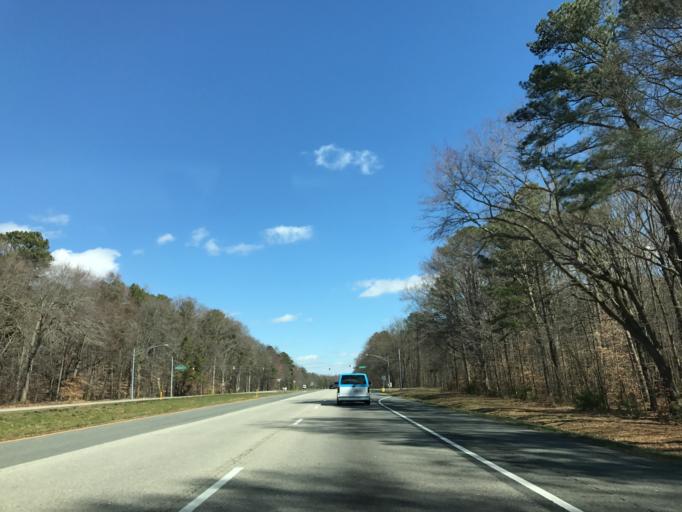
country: US
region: Maryland
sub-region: Queen Anne's County
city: Centreville
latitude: 39.0067
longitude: -76.1135
